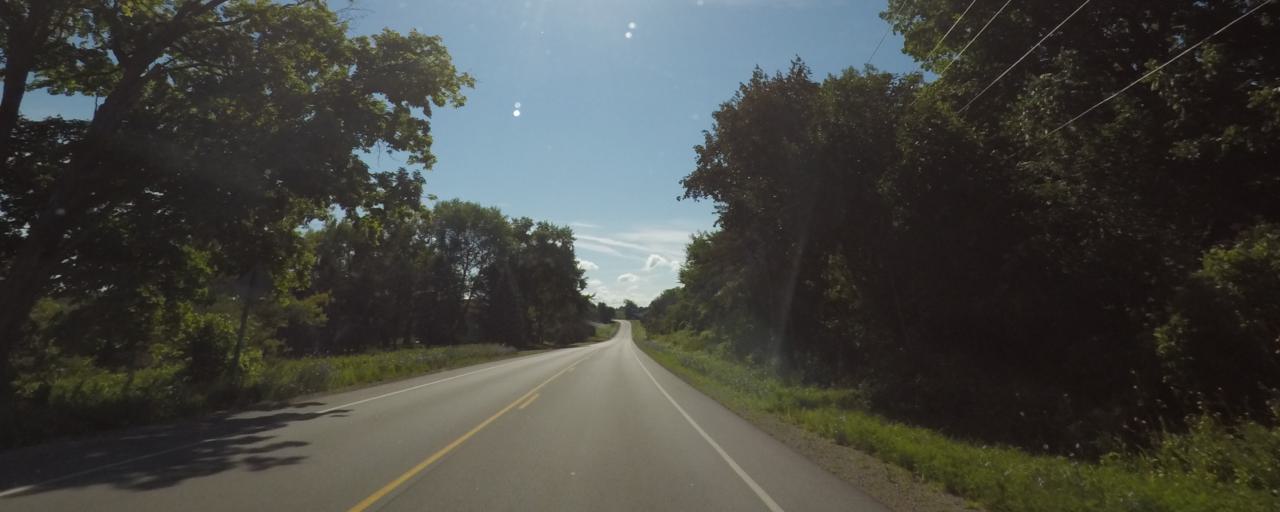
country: US
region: Wisconsin
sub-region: Jefferson County
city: Johnson Creek
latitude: 43.0730
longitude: -88.7059
